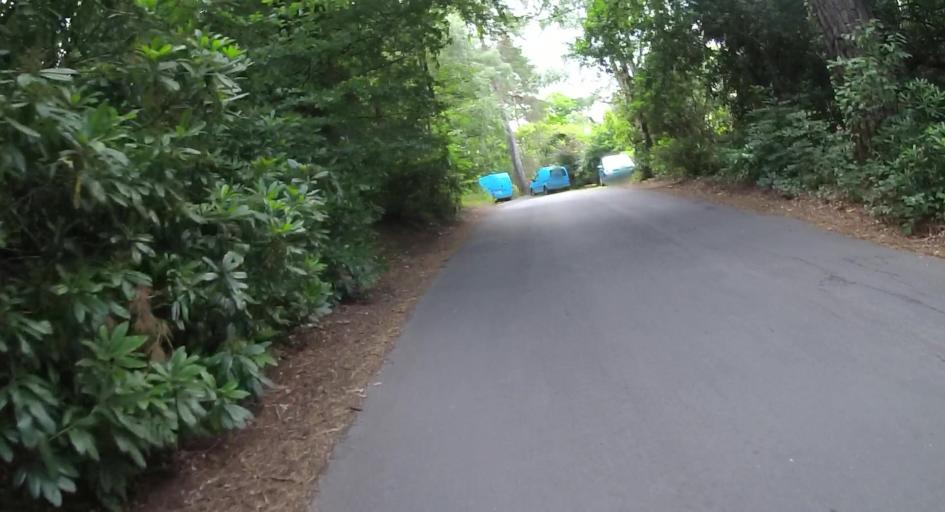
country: GB
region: England
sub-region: Surrey
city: Seale
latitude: 51.2102
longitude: -0.7536
